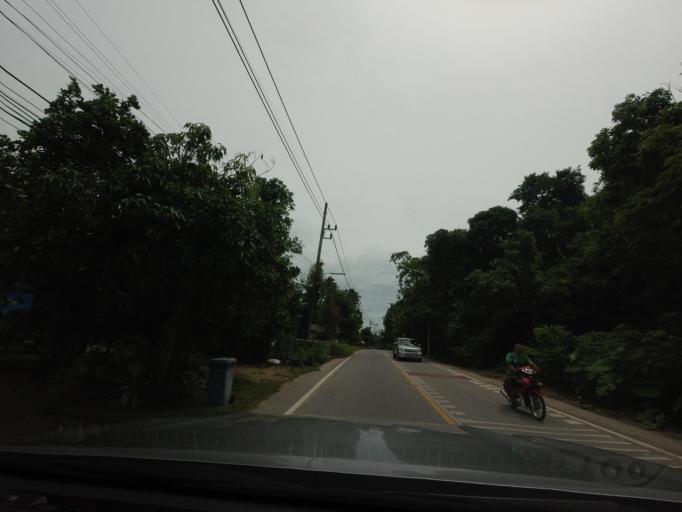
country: TH
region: Pattani
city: Kapho
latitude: 6.5835
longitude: 101.5346
